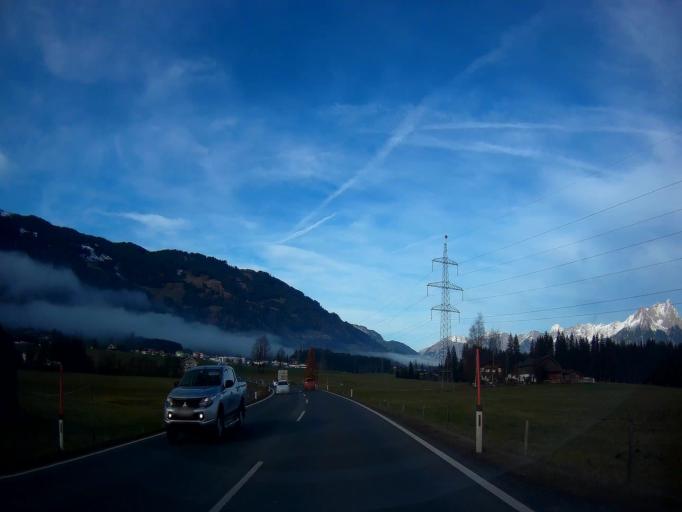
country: AT
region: Salzburg
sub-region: Politischer Bezirk Zell am See
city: Maishofen
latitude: 47.3832
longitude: 12.8080
